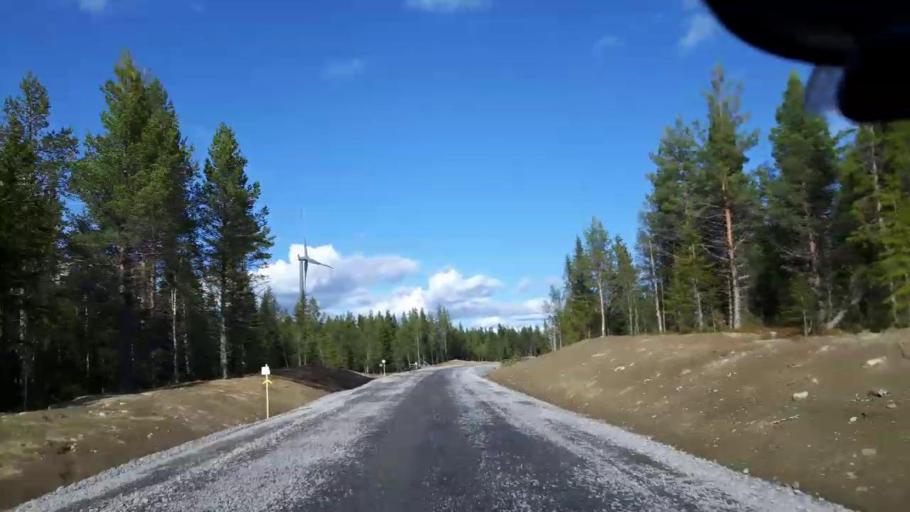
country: SE
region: Jaemtland
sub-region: Ragunda Kommun
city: Hammarstrand
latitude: 63.4226
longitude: 16.1203
